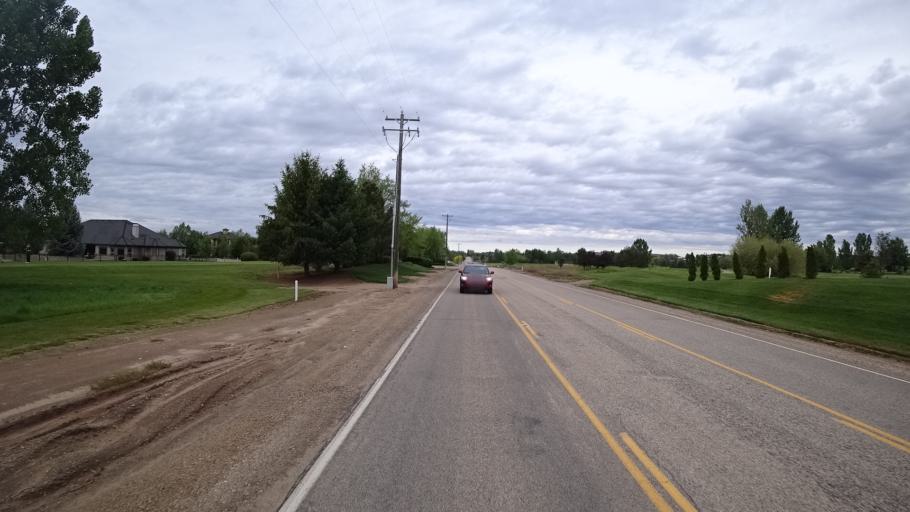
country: US
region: Idaho
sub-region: Ada County
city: Star
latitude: 43.7211
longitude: -116.4633
